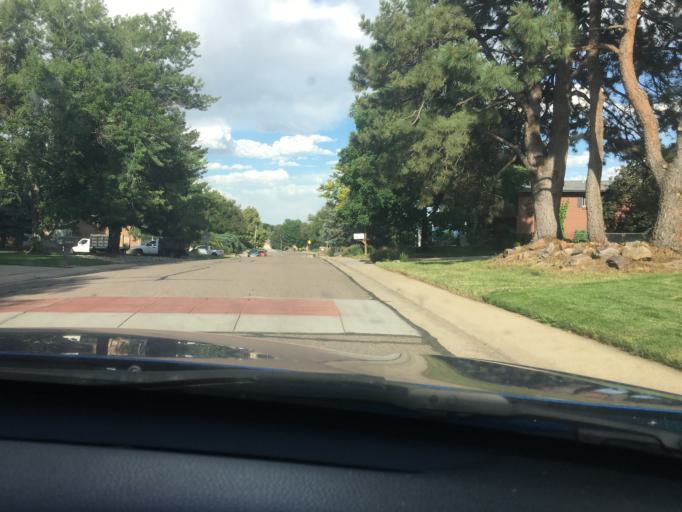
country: US
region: Colorado
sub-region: Jefferson County
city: Applewood
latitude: 39.7655
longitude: -105.1348
